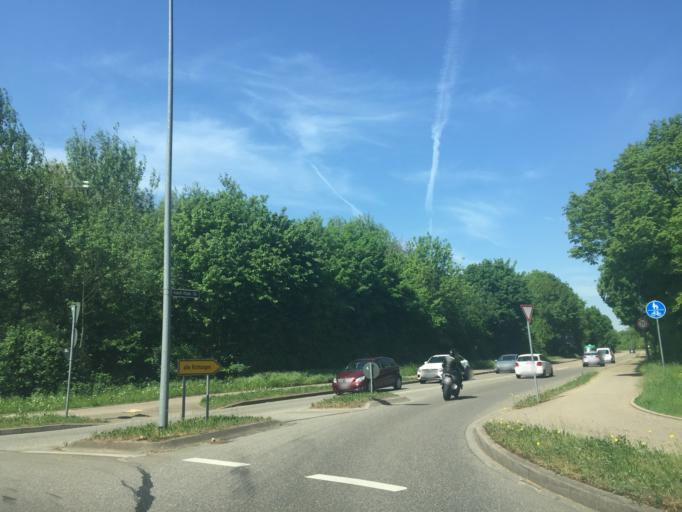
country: DE
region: Baden-Wuerttemberg
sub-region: Karlsruhe Region
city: Ettlingen
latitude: 48.9346
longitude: 8.3757
